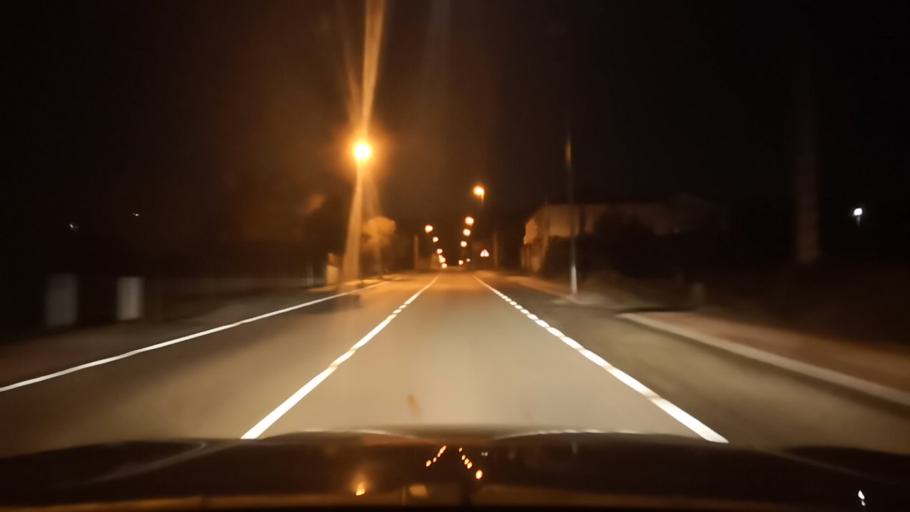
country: ES
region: Galicia
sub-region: Provincia de Ourense
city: Verin
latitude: 41.9383
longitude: -7.4173
